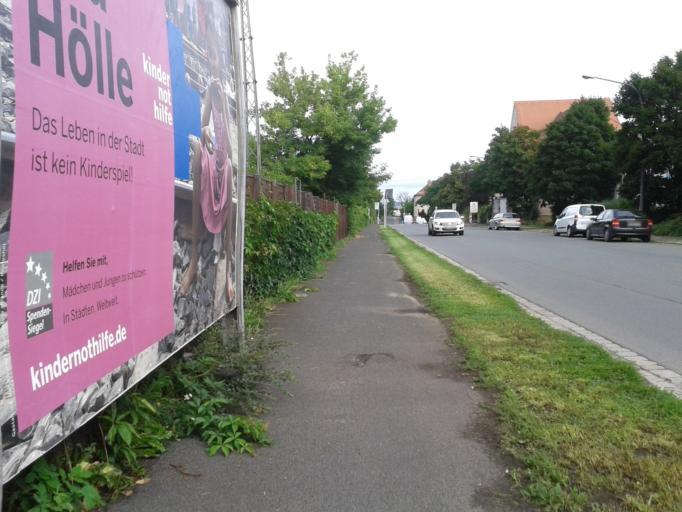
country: DE
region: Bavaria
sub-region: Upper Franconia
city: Bamberg
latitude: 49.8882
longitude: 10.9139
